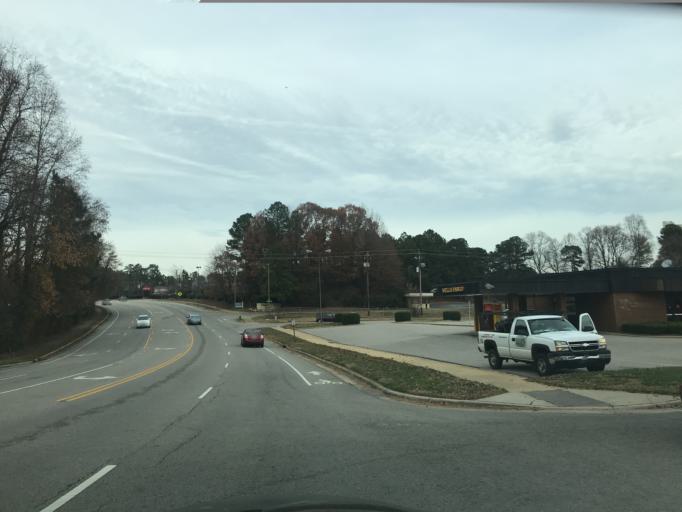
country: US
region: North Carolina
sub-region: Wake County
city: West Raleigh
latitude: 35.7859
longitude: -78.7030
